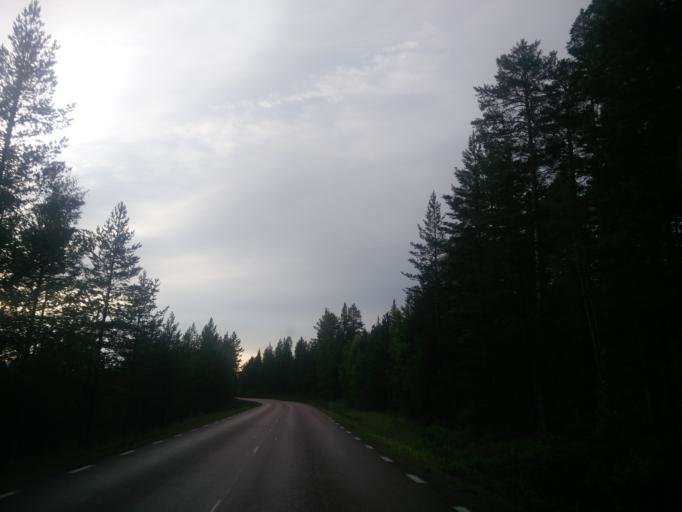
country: NO
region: Hedmark
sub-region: Trysil
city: Innbygda
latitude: 61.7844
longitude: 12.9352
